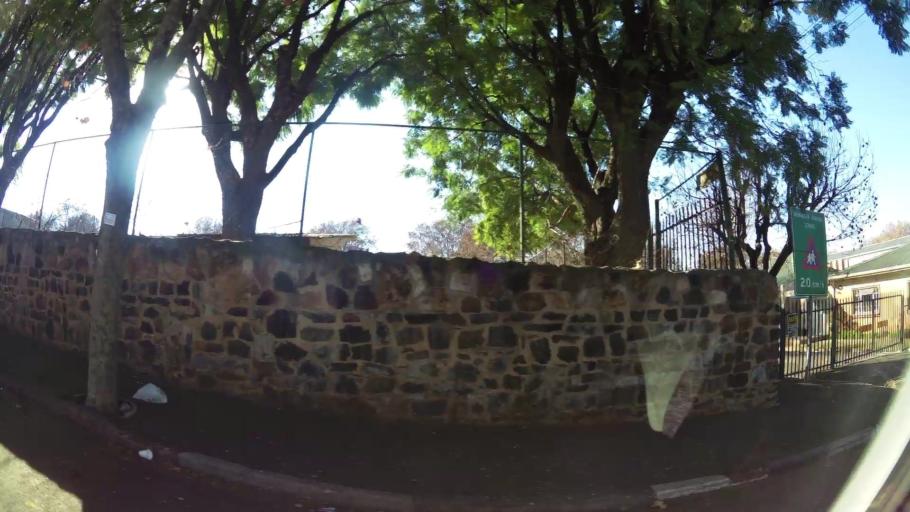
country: ZA
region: Gauteng
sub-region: City of Johannesburg Metropolitan Municipality
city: Johannesburg
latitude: -26.2044
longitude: 28.0745
